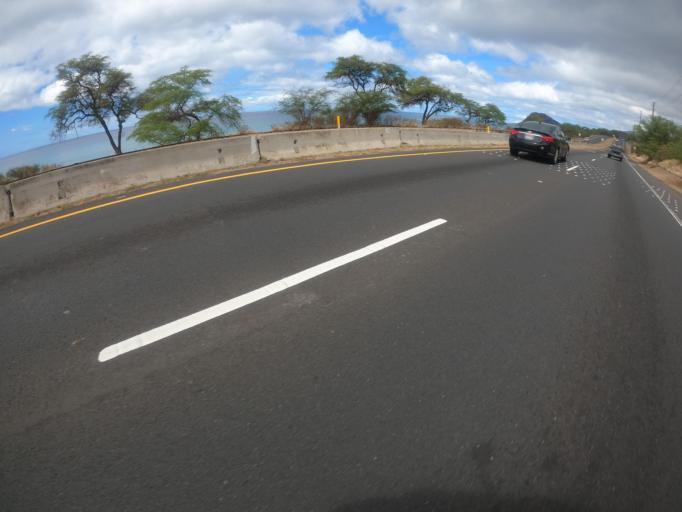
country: US
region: Hawaii
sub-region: Honolulu County
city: Nanakuli
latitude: 21.3642
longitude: -158.1334
